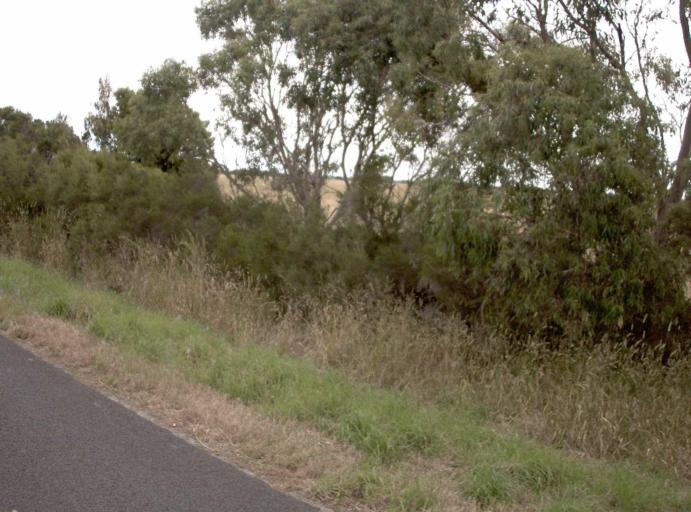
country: AU
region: Victoria
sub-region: Wellington
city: Sale
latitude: -38.5975
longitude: 146.8869
